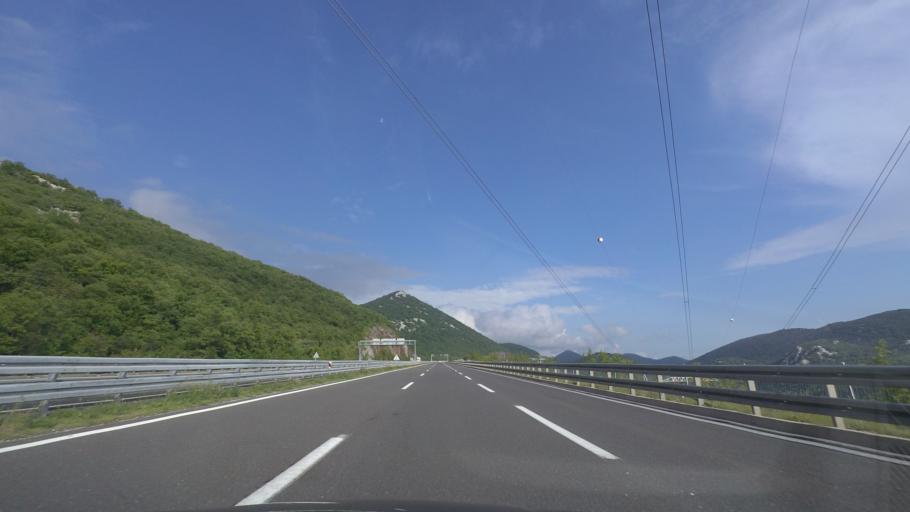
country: HR
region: Primorsko-Goranska
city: Cernik
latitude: 45.3753
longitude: 14.5371
